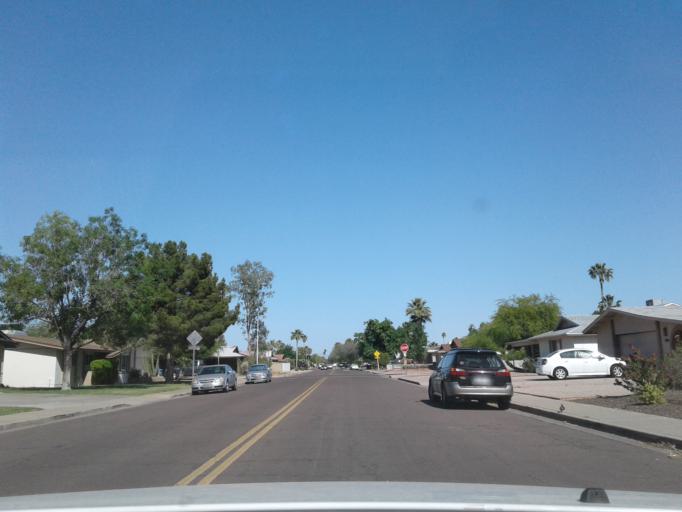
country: US
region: Arizona
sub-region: Maricopa County
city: Tempe
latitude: 33.4001
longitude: -111.9050
